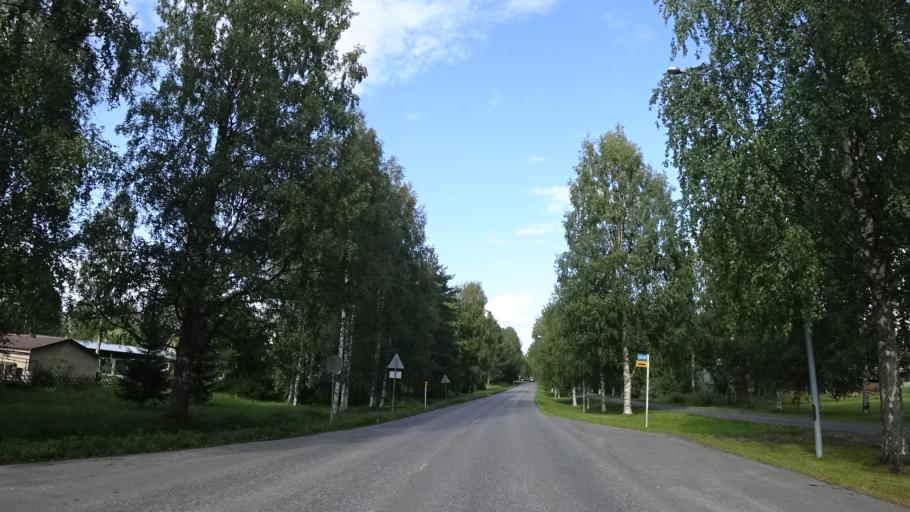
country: FI
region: North Karelia
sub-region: Pielisen Karjala
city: Lieksa
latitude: 63.3297
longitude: 30.0251
